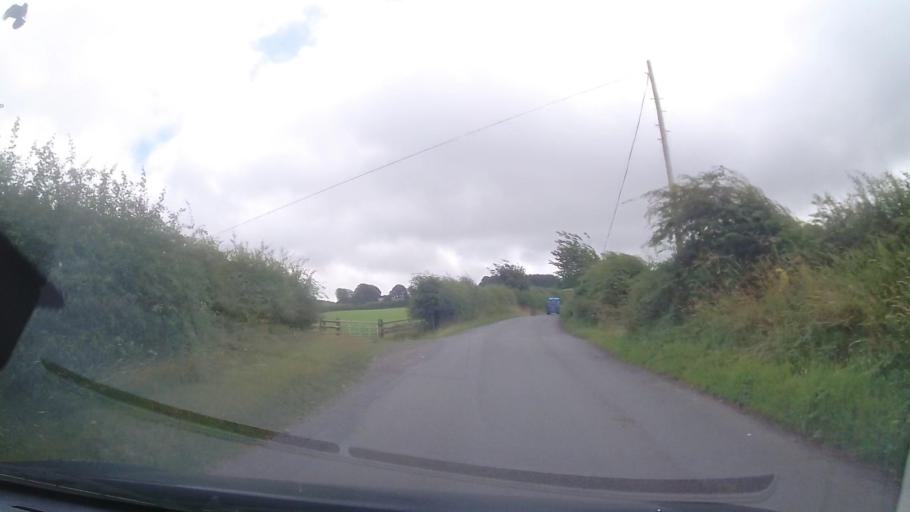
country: GB
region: Wales
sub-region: Sir Powys
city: Knighton
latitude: 52.3382
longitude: -3.0296
